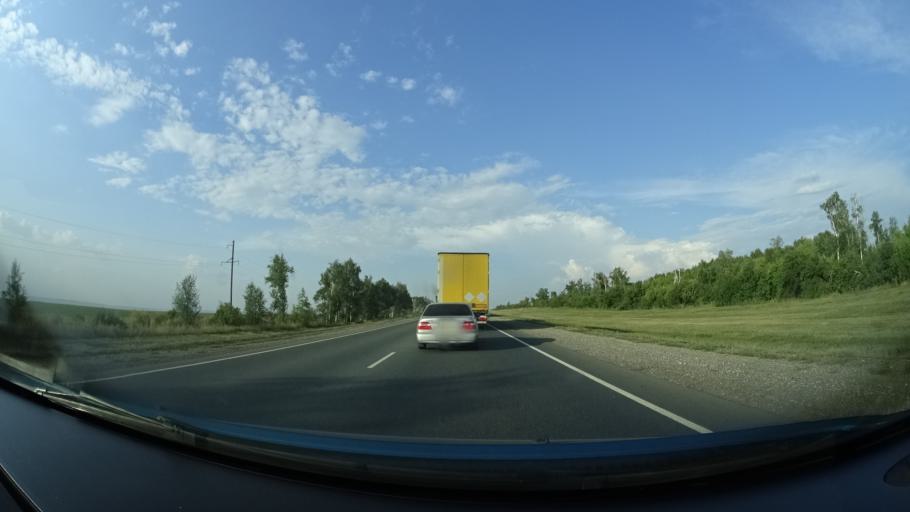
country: RU
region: Samara
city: Krasnyy Yar
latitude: 53.6685
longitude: 50.7637
